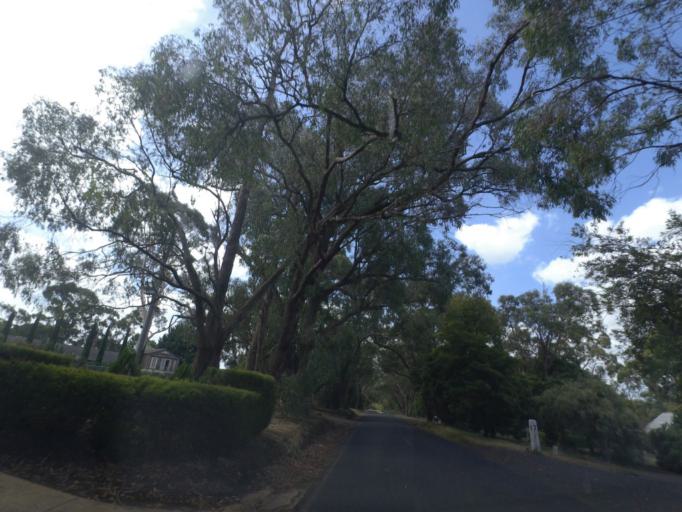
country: AU
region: Victoria
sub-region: Yarra Ranges
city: Lilydale
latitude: -37.7797
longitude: 145.3501
